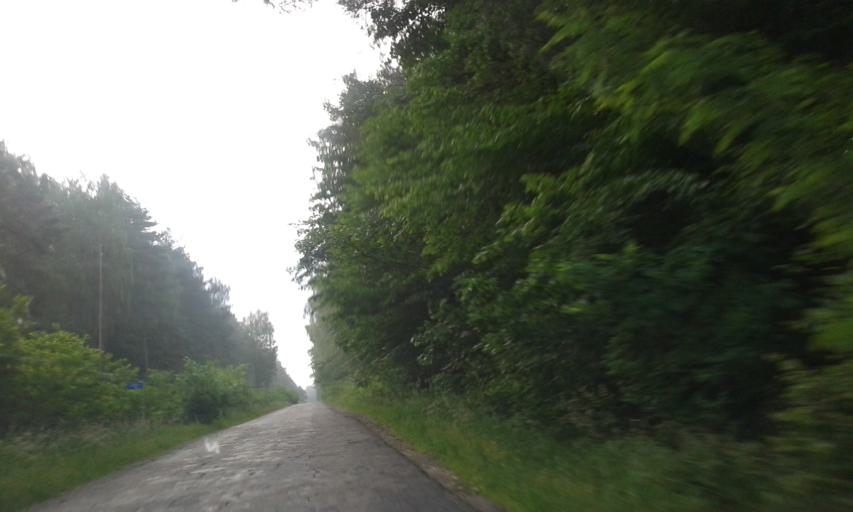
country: PL
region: Kujawsko-Pomorskie
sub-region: Powiat sepolenski
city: Sypniewo
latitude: 53.4502
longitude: 17.3906
